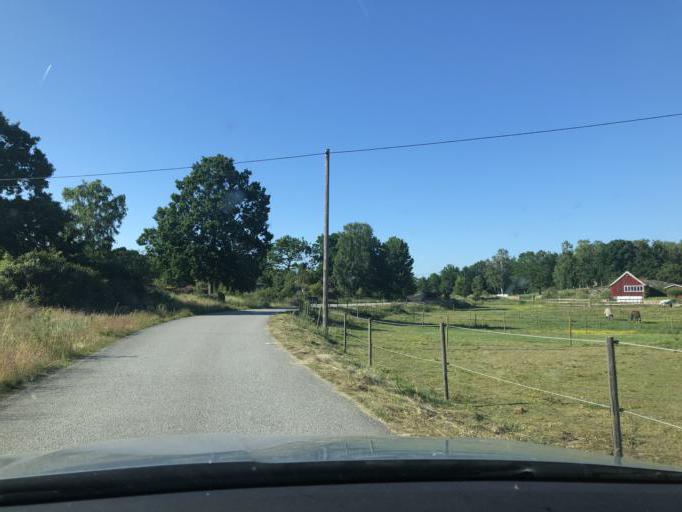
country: SE
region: Blekinge
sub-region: Karlshamns Kommun
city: Morrum
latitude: 56.1585
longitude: 14.7999
